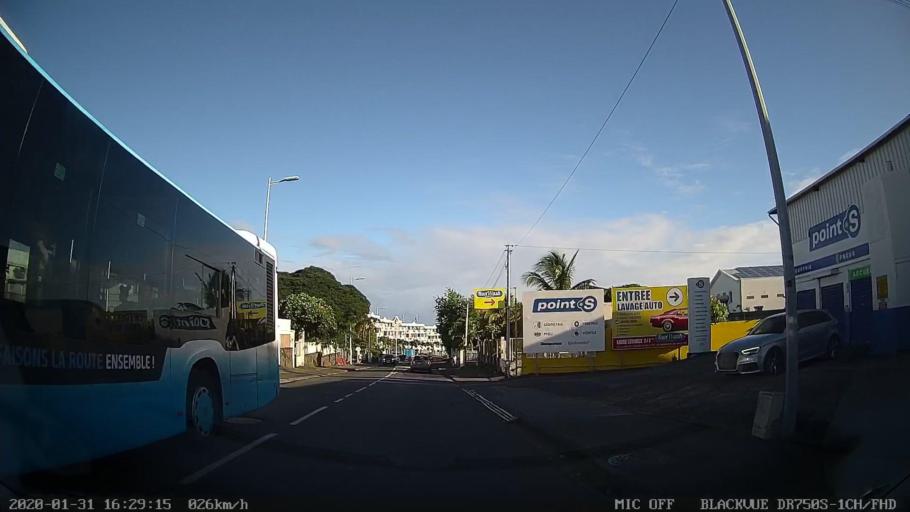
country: RE
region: Reunion
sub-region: Reunion
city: Saint-Denis
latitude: -20.8991
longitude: 55.4918
